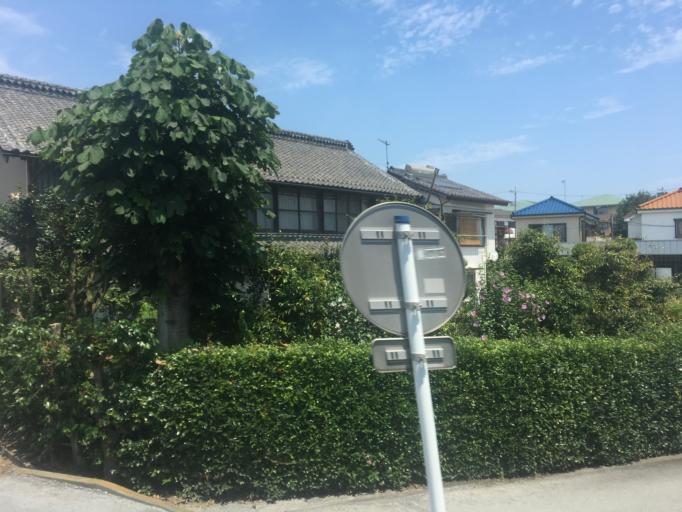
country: JP
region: Saitama
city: Yorii
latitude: 36.1553
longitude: 139.1998
